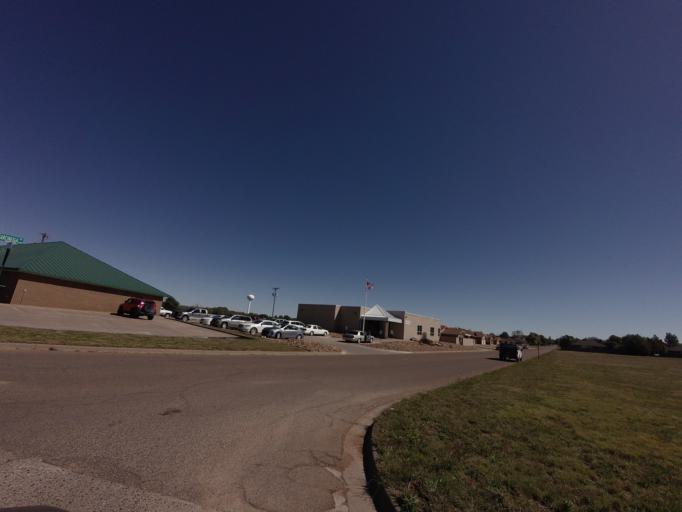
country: US
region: New Mexico
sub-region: Curry County
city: Clovis
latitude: 34.4261
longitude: -103.1920
